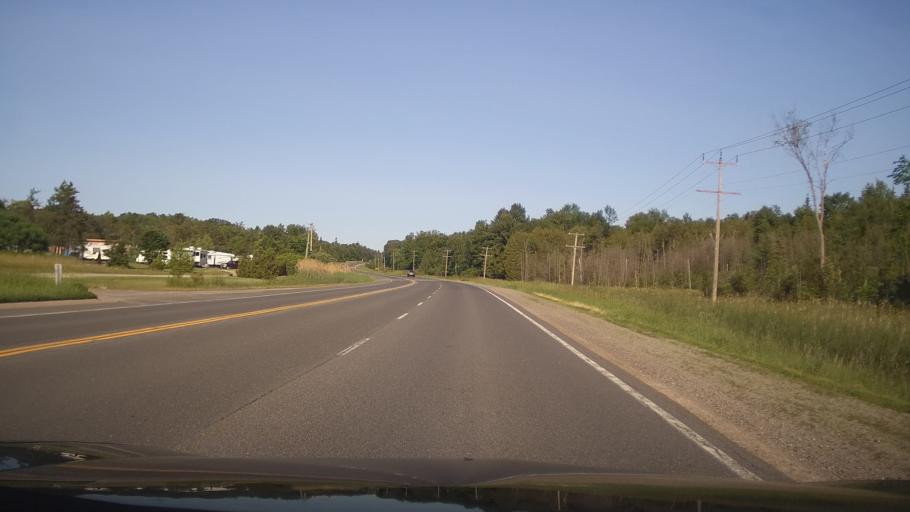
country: CA
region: Ontario
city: Quinte West
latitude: 44.5033
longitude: -77.5165
